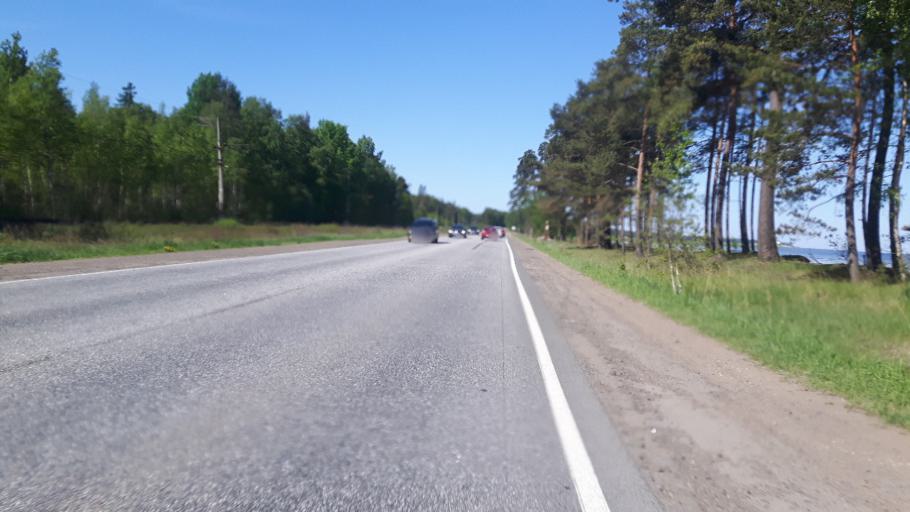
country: RU
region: Leningrad
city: Lebyazh'ye
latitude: 59.9570
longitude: 29.4876
